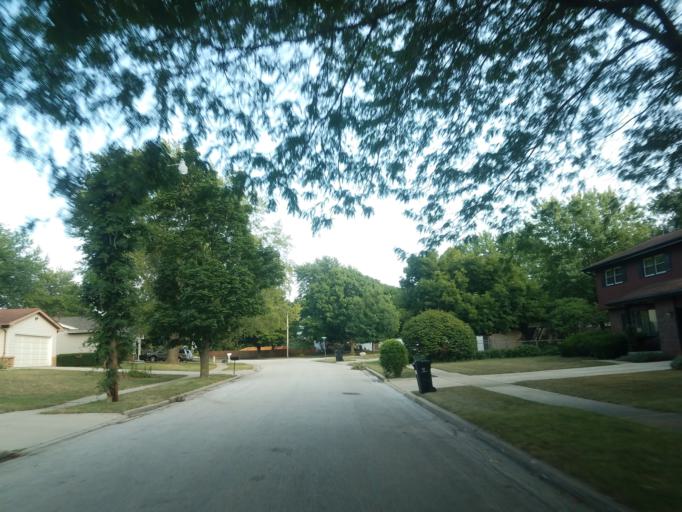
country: US
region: Illinois
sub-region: McLean County
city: Bloomington
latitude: 40.4693
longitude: -88.9444
